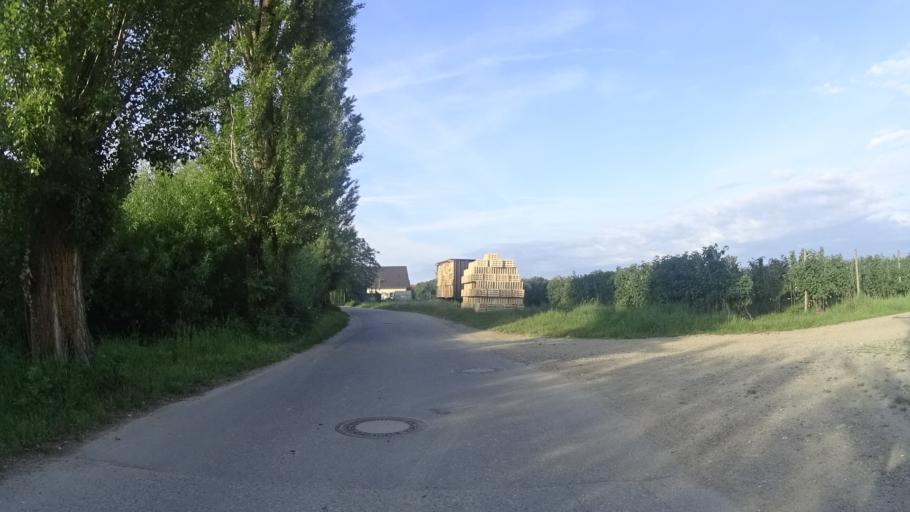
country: DE
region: Baden-Wuerttemberg
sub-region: Freiburg Region
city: Hartheim
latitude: 47.9402
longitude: 7.6474
